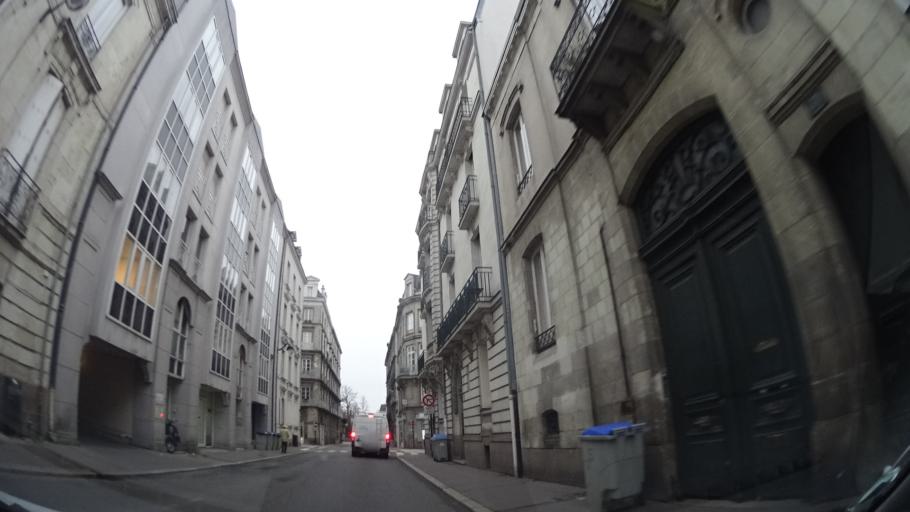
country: FR
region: Pays de la Loire
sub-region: Departement de la Loire-Atlantique
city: Nantes
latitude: 47.2155
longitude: -1.5665
